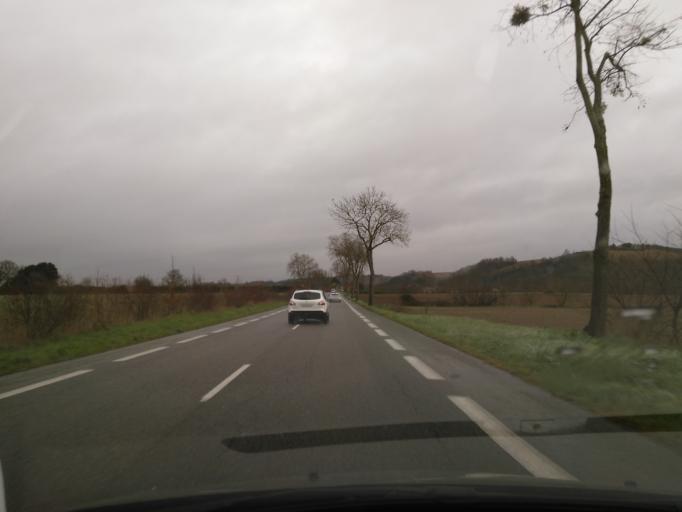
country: FR
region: Midi-Pyrenees
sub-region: Departement de la Haute-Garonne
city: Rieux-Volvestre
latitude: 43.2769
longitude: 1.2072
